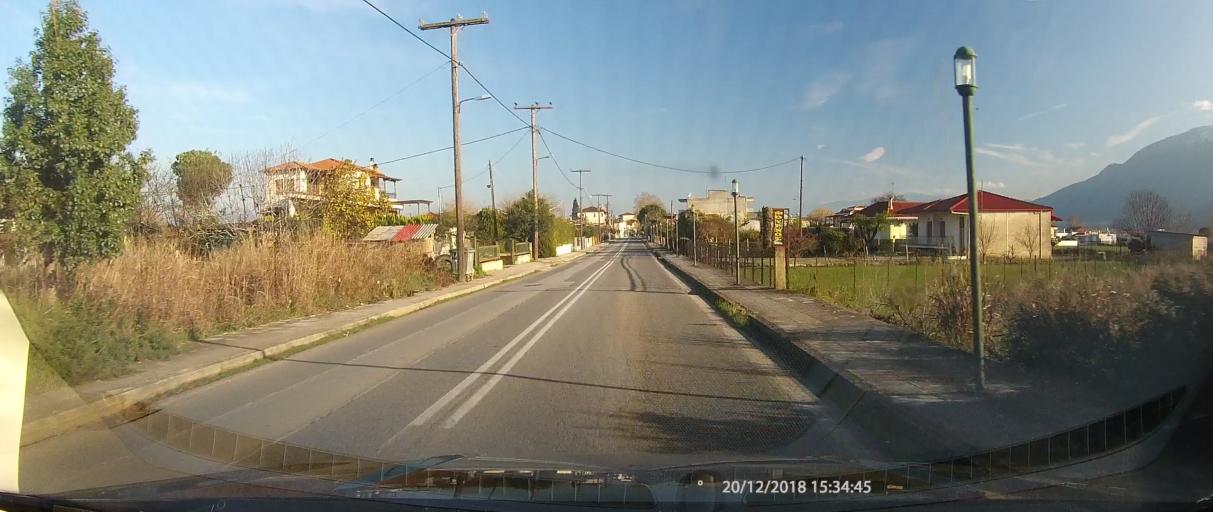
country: GR
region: Central Greece
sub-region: Nomos Fthiotidos
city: Lianokladhion
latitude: 38.9179
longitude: 22.2981
